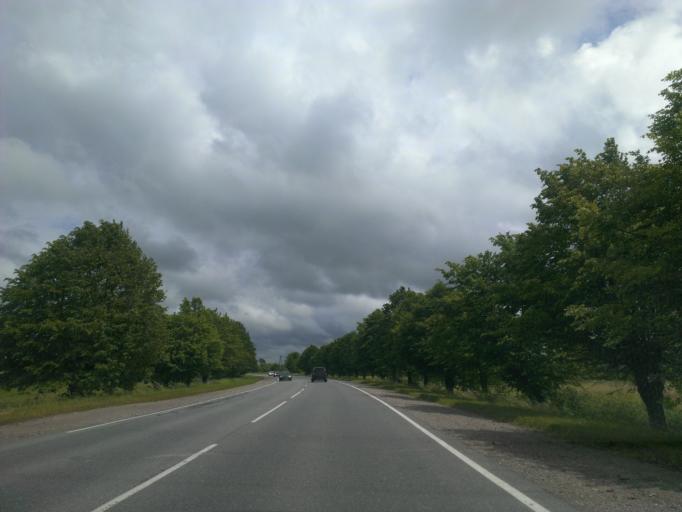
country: LV
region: Grobina
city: Grobina
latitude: 56.5326
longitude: 21.1130
